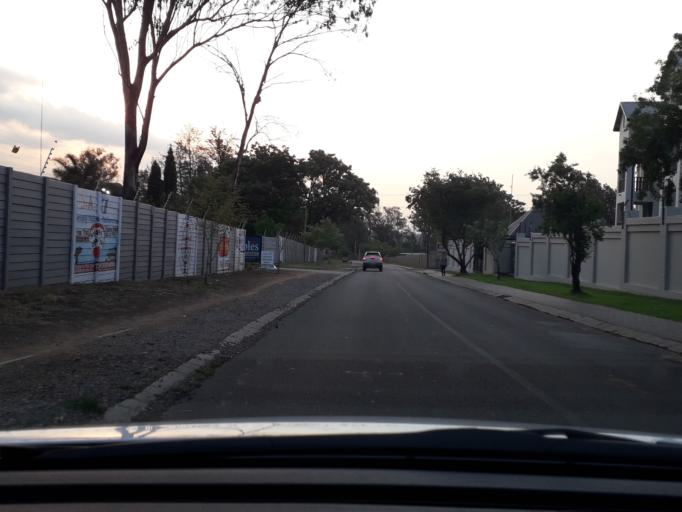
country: ZA
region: Gauteng
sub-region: City of Johannesburg Metropolitan Municipality
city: Diepsloot
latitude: -25.9947
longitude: 27.9817
